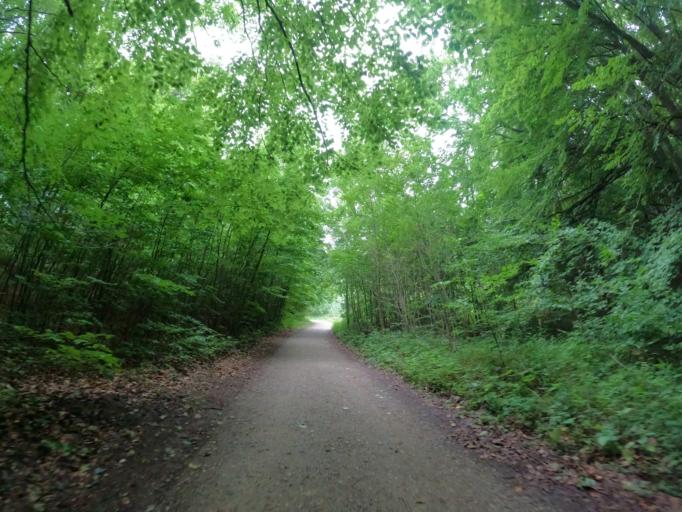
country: DE
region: Mecklenburg-Vorpommern
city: Putbus
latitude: 54.3414
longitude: 13.5220
